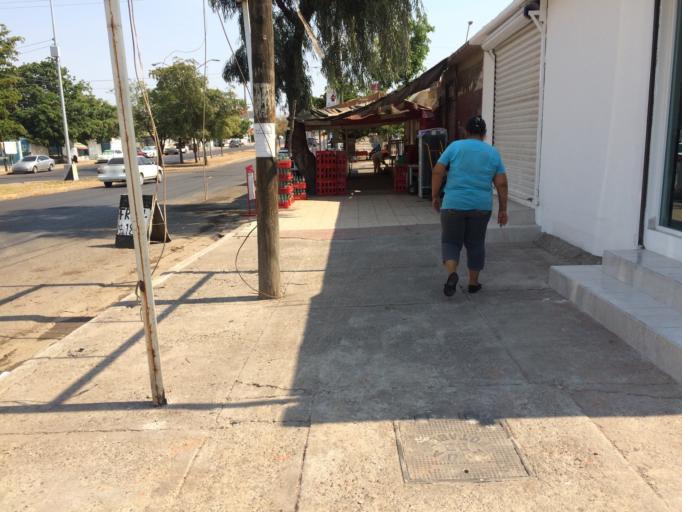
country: MX
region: Sinaloa
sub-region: Culiacan
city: El Diez
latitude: 24.7555
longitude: -107.4289
